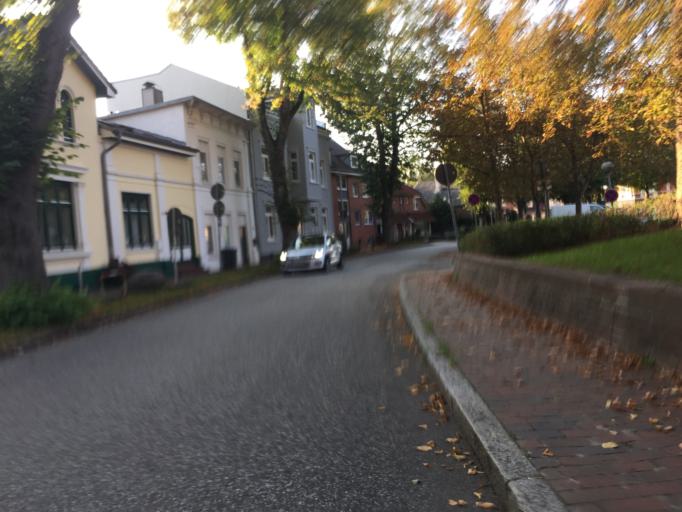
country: DE
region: Schleswig-Holstein
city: Itzehoe
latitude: 53.9189
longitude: 9.5217
